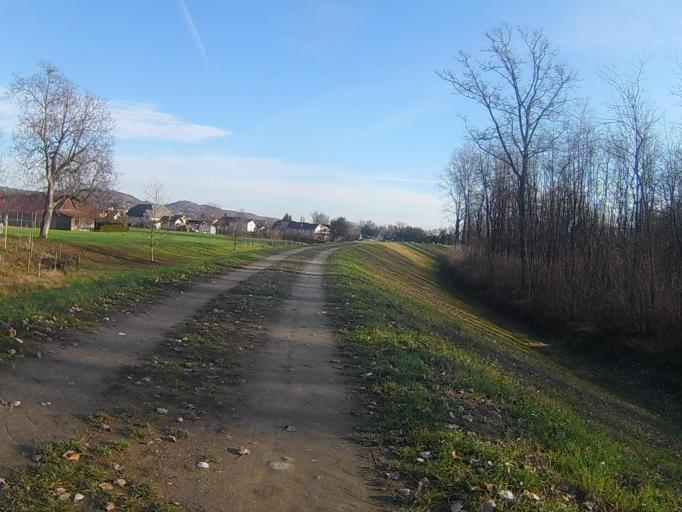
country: SI
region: Duplek
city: Spodnji Duplek
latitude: 46.5051
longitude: 15.7393
